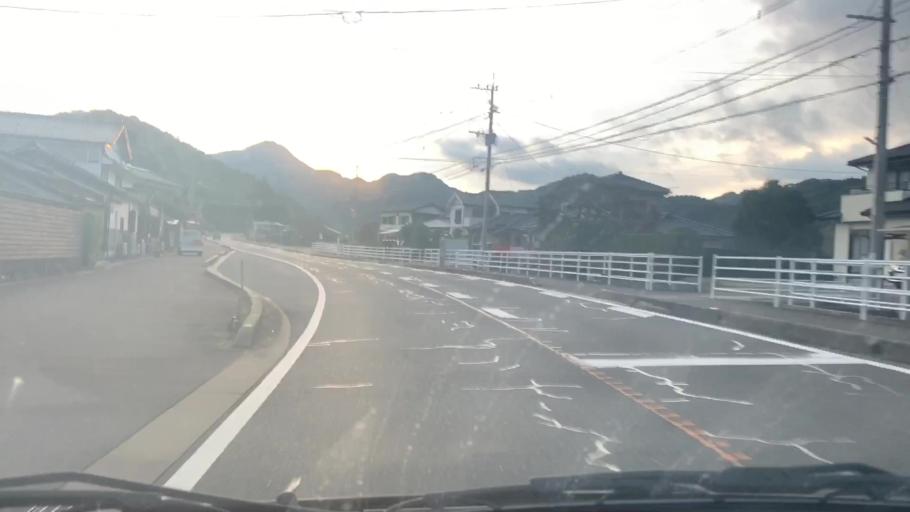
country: JP
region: Saga Prefecture
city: Kashima
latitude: 33.0886
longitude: 130.0819
